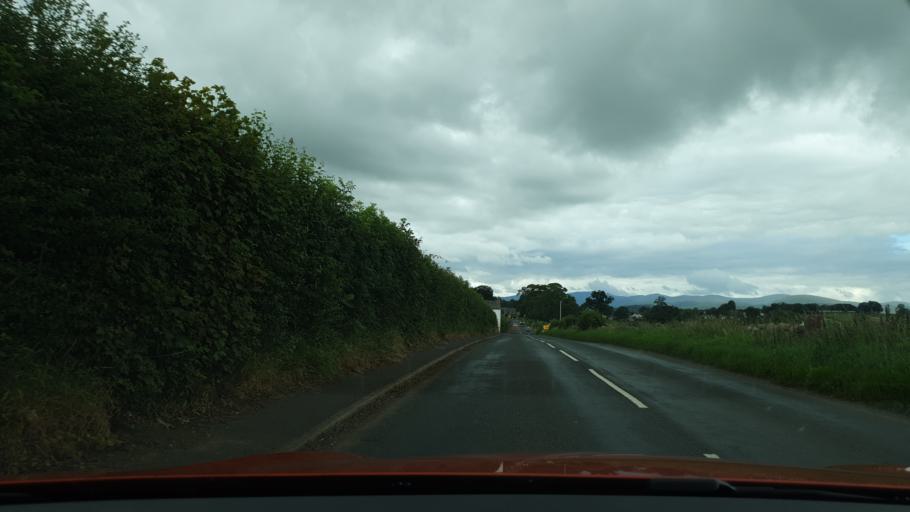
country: GB
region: England
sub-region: Cumbria
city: Penrith
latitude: 54.6374
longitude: -2.7631
